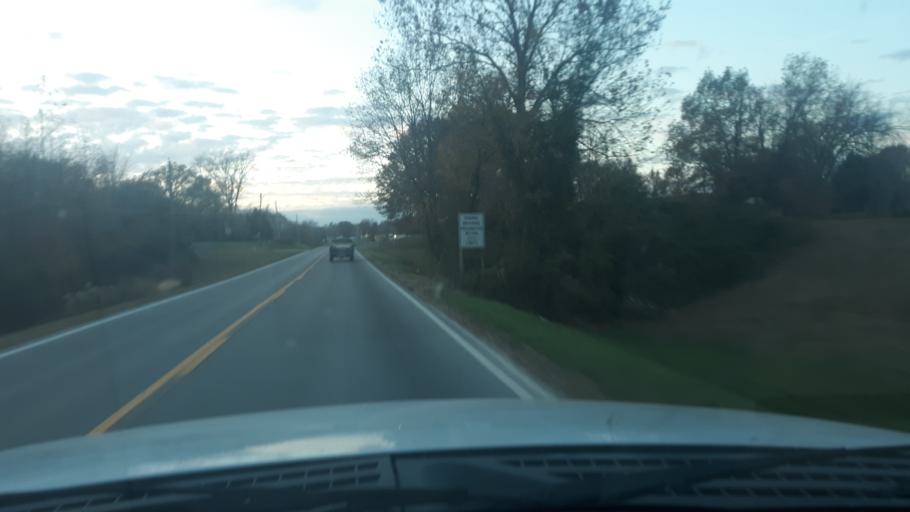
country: US
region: Illinois
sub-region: Saline County
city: Harrisburg
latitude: 37.8372
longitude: -88.5947
